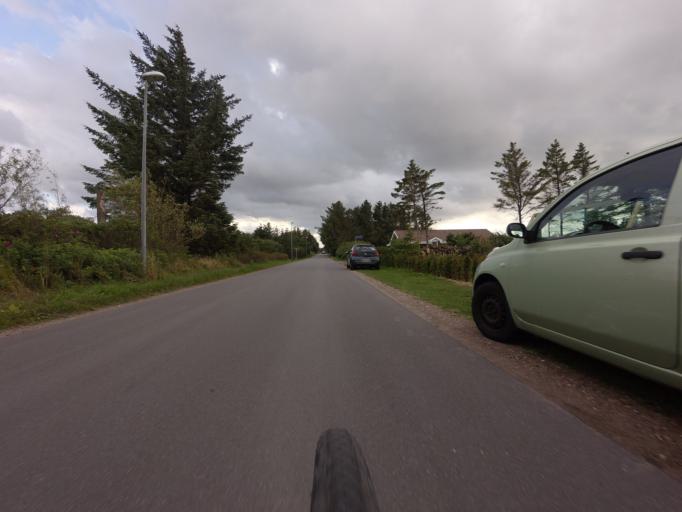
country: DK
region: North Denmark
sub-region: Hjorring Kommune
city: Hjorring
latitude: 57.4725
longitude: 9.8076
